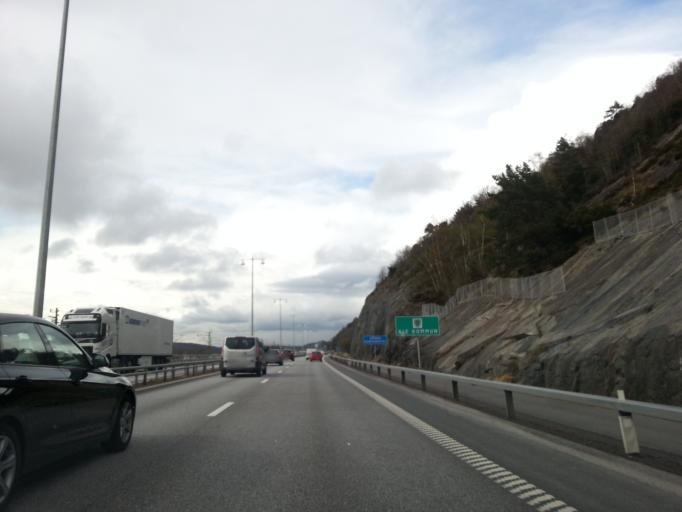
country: SE
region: Vaestra Goetaland
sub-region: Goteborg
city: Gardsten
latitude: 57.8045
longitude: 12.0164
